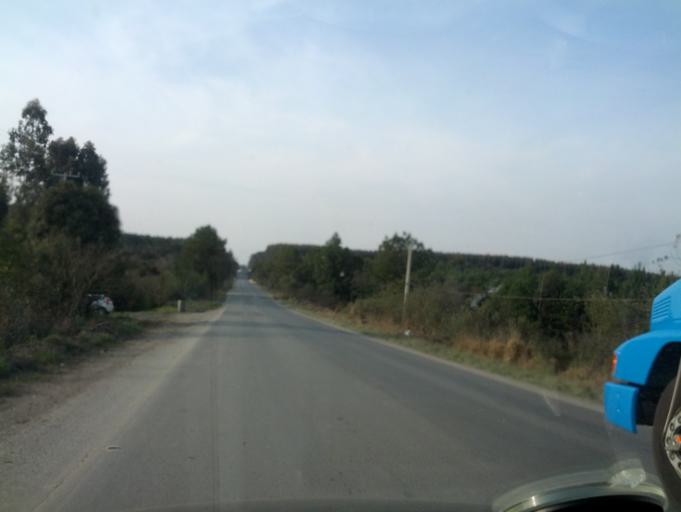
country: BR
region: Santa Catarina
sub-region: Otacilio Costa
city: Otacilio Costa
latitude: -27.5187
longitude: -50.1340
